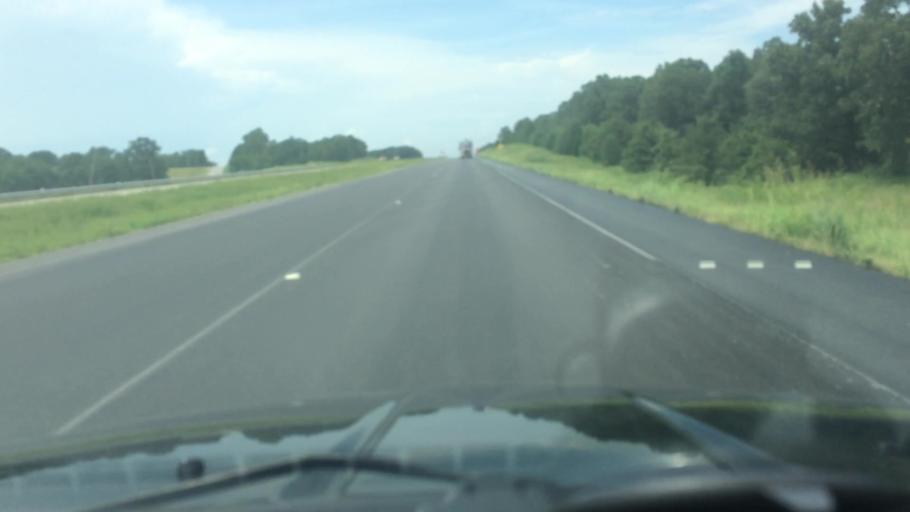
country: US
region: Missouri
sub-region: Saint Clair County
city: Osceola
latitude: 37.9617
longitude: -93.6437
